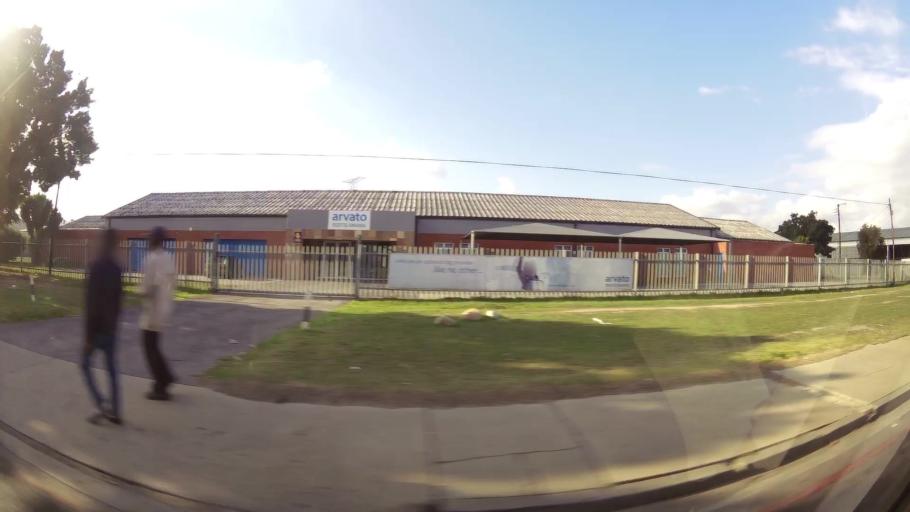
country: ZA
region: Eastern Cape
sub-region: Nelson Mandela Bay Metropolitan Municipality
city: Uitenhage
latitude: -33.7818
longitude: 25.4160
